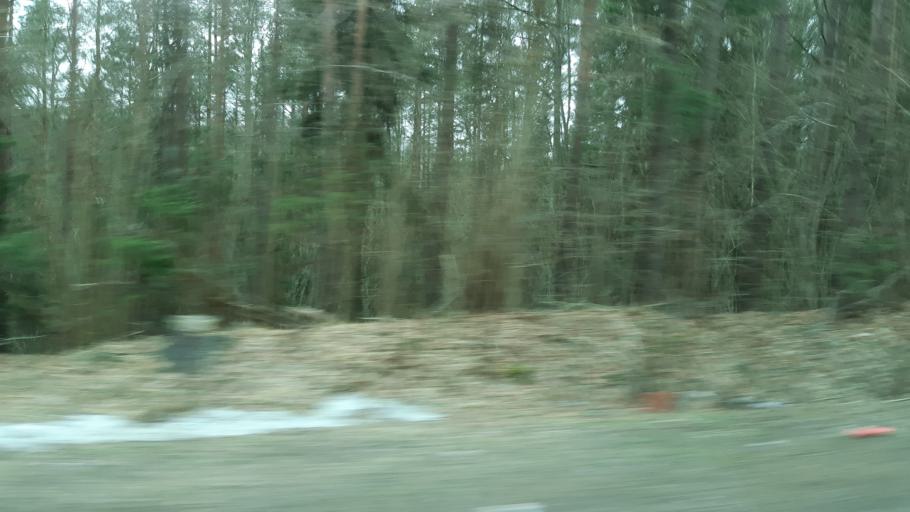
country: PL
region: Podlasie
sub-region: Suwalki
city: Suwalki
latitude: 54.2863
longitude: 22.9530
